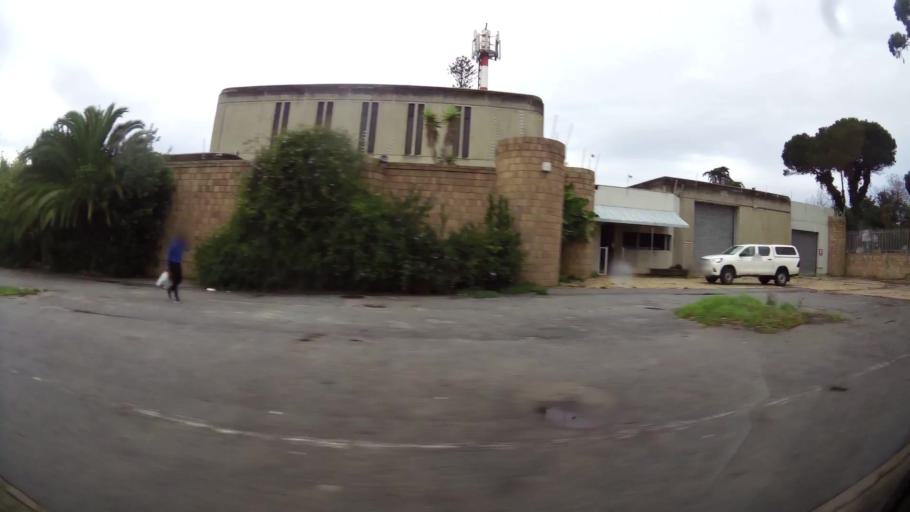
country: ZA
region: Eastern Cape
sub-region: Nelson Mandela Bay Metropolitan Municipality
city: Port Elizabeth
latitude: -33.9809
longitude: 25.5788
